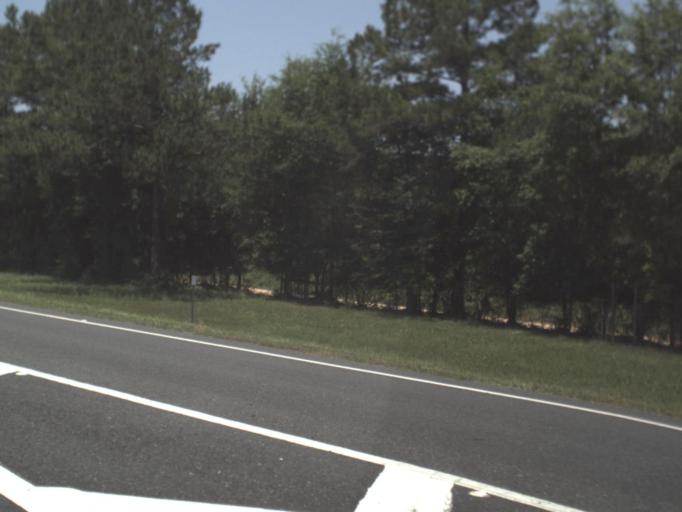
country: US
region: Florida
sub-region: Baker County
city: Macclenny
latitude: 30.2618
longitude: -82.1647
